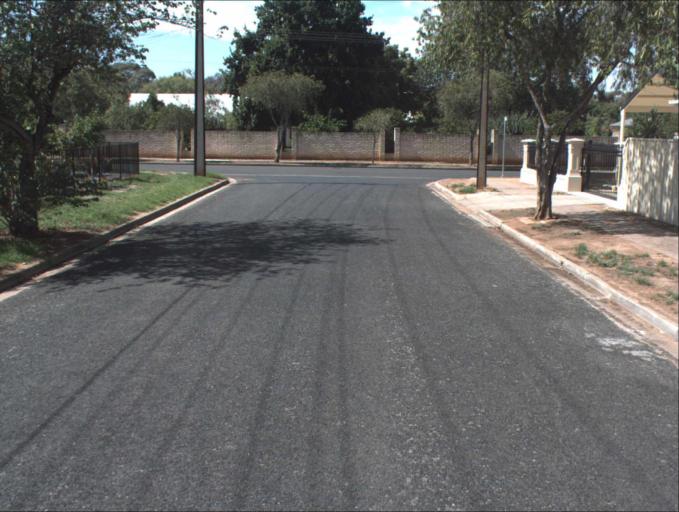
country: AU
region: South Australia
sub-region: Port Adelaide Enfield
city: Klemzig
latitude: -34.8814
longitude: 138.6452
